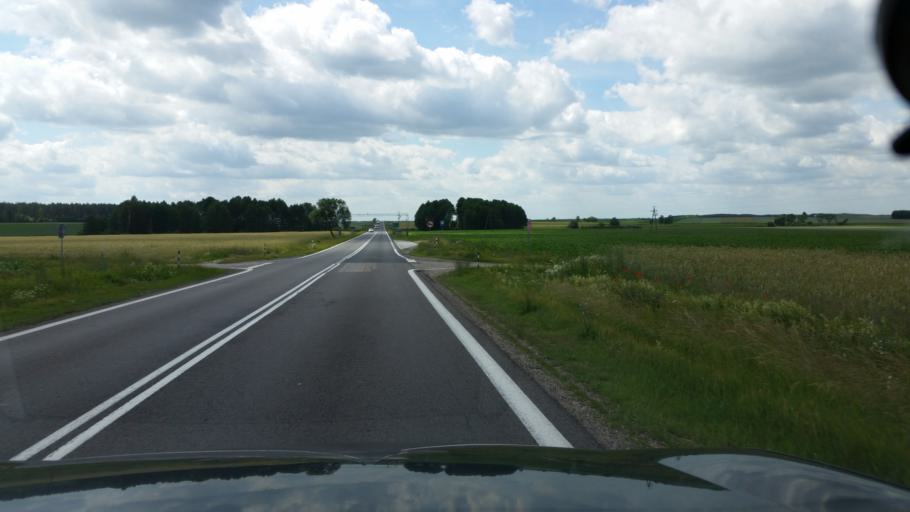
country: PL
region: Podlasie
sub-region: Powiat kolnenski
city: Stawiski
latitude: 53.4203
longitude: 22.1662
